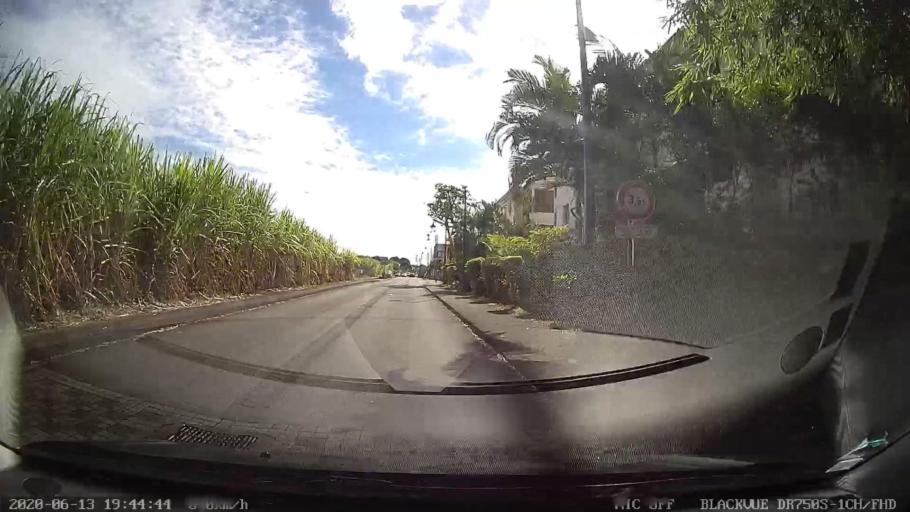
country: RE
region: Reunion
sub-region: Reunion
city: Bras-Panon
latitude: -21.0005
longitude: 55.6765
